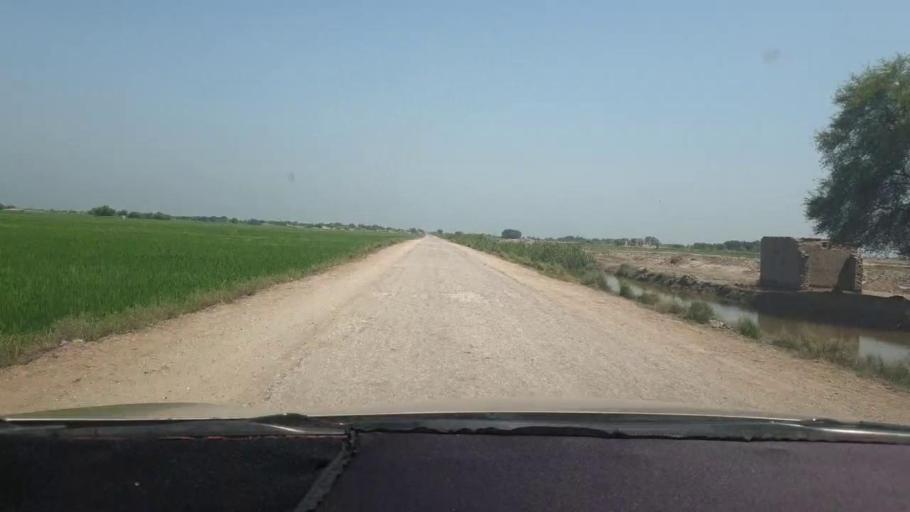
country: PK
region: Sindh
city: Miro Khan
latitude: 27.6889
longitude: 68.0819
